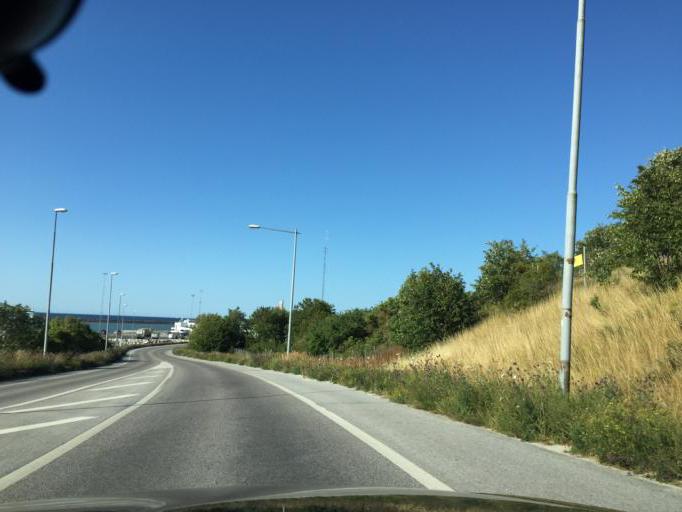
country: SE
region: Gotland
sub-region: Gotland
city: Visby
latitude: 57.6269
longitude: 18.2745
